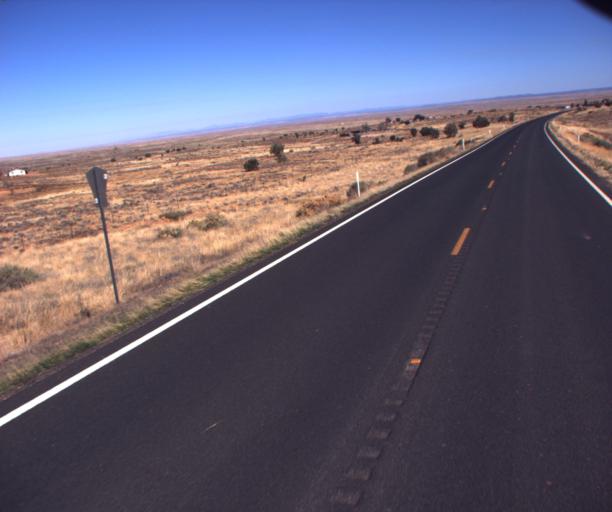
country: US
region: Arizona
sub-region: Apache County
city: Ganado
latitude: 35.7794
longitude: -109.7271
